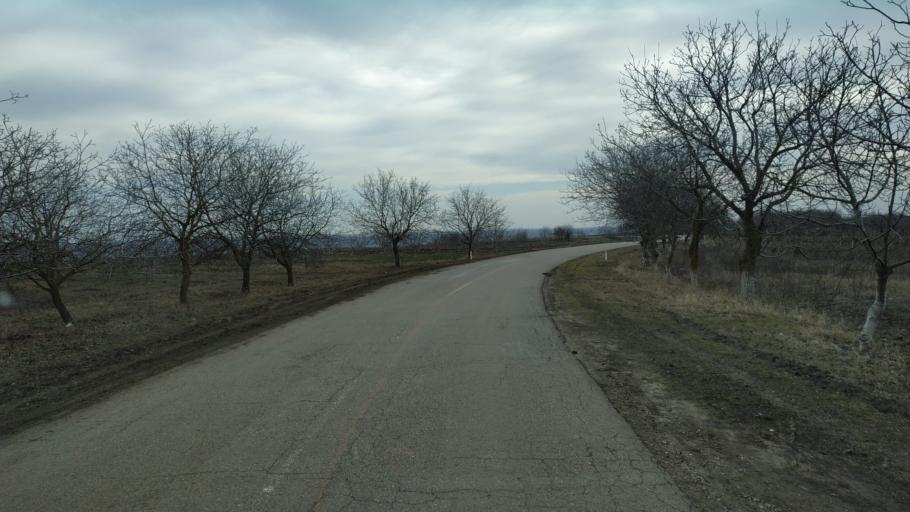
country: MD
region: Nisporeni
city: Nisporeni
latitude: 46.9461
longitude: 28.2420
